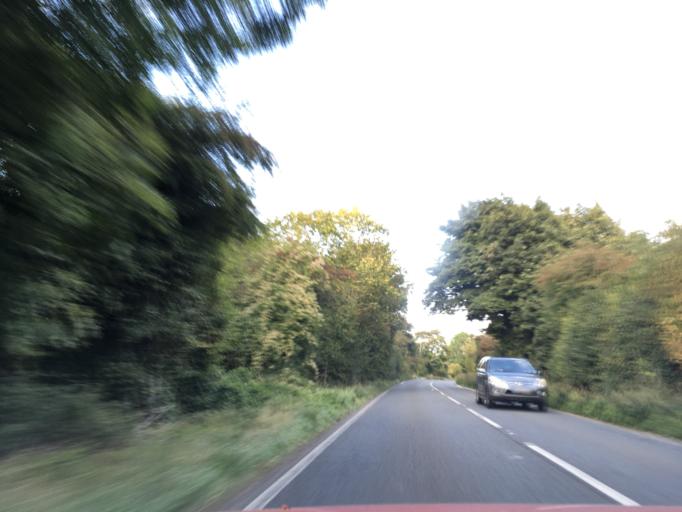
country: GB
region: England
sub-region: Gloucestershire
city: Northleach
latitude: 51.8484
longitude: -1.8210
